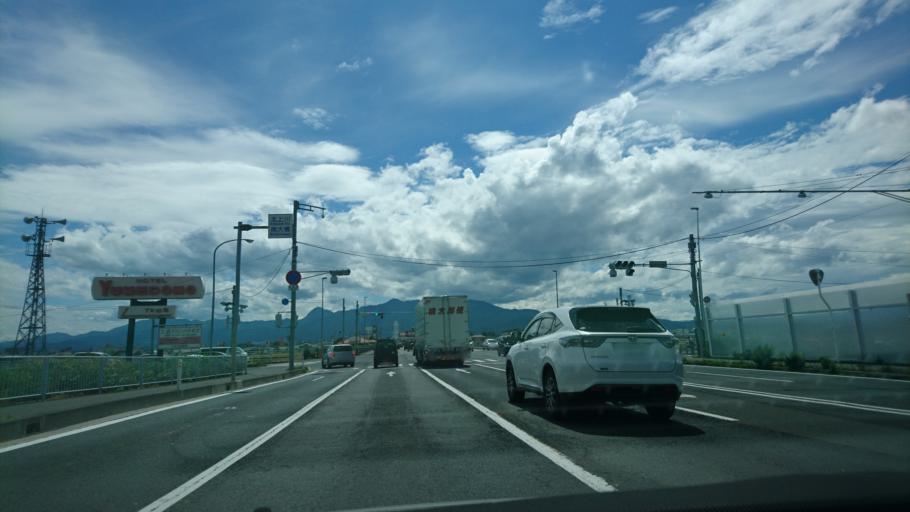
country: JP
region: Iwate
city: Morioka-shi
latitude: 39.6855
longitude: 141.1620
